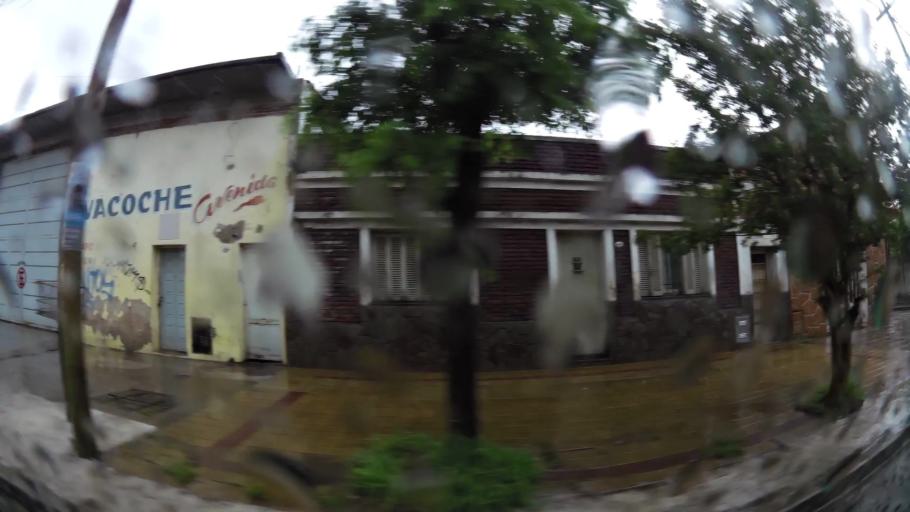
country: AR
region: Buenos Aires
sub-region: Partido de Lanus
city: Lanus
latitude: -34.7174
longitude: -58.4064
